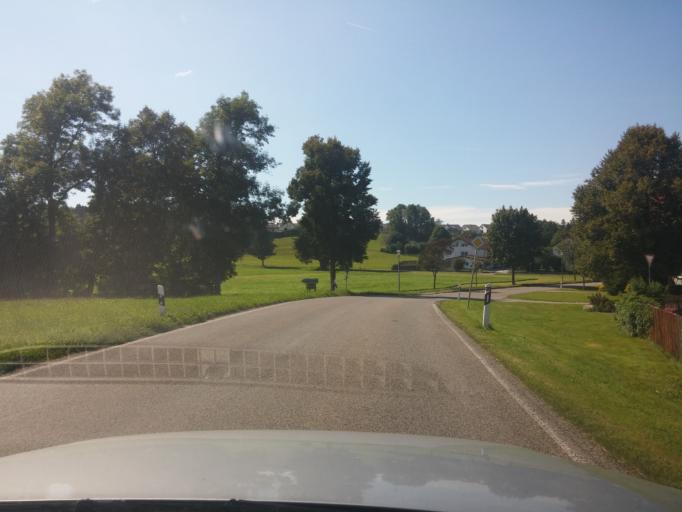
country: DE
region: Baden-Wuerttemberg
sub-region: Tuebingen Region
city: Leutkirch im Allgau
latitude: 47.8168
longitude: 10.0602
